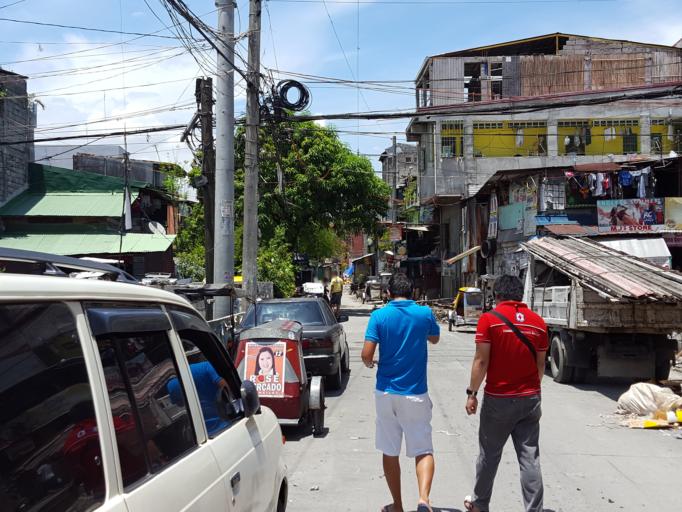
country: PH
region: Metro Manila
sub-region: Caloocan City
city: Niugan
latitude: 14.6478
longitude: 120.9699
